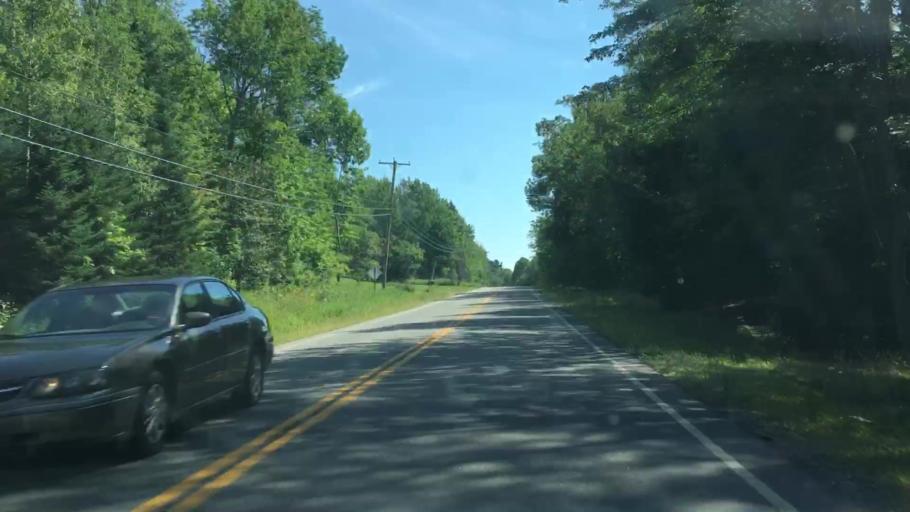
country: US
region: Maine
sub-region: Piscataquis County
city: Milo
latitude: 45.1981
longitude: -68.9048
